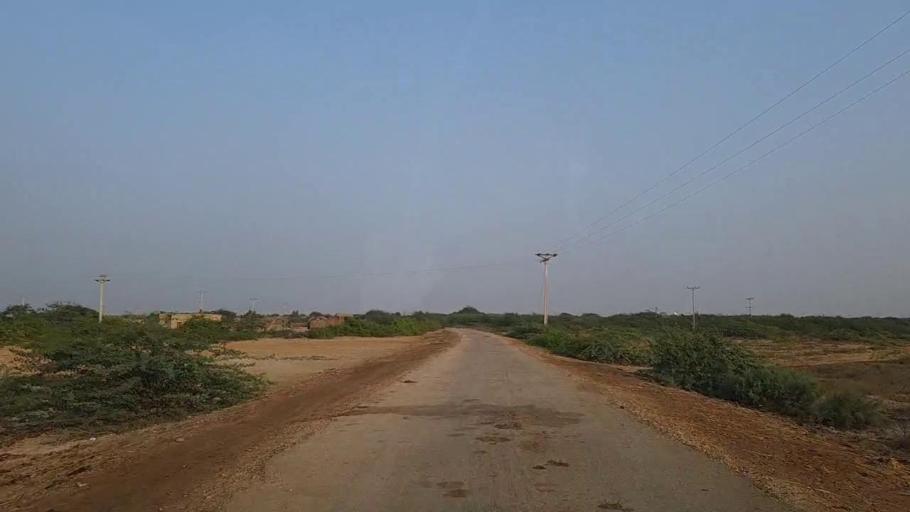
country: PK
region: Sindh
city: Thatta
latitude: 24.6901
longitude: 67.8148
